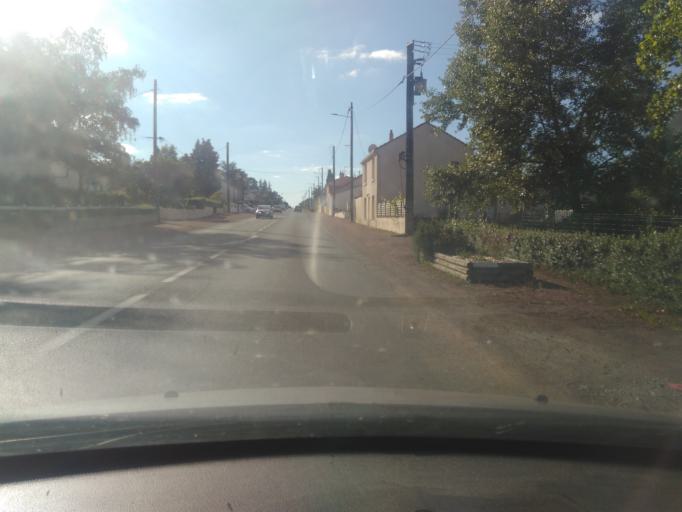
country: FR
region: Pays de la Loire
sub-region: Departement de la Vendee
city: Saint-Florent-des-Bois
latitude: 46.5977
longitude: -1.3228
